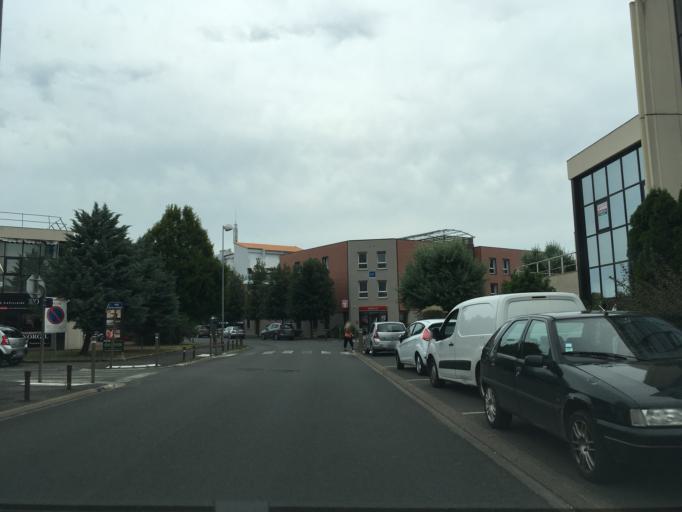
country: FR
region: Poitou-Charentes
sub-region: Departement des Deux-Sevres
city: Niort
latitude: 46.3167
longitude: -0.4717
